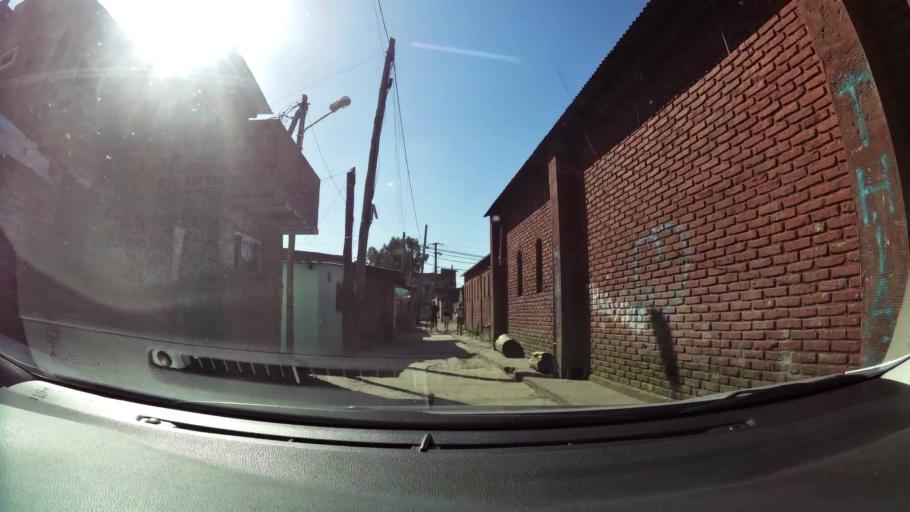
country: AR
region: Buenos Aires F.D.
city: Villa Lugano
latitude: -34.7073
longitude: -58.4879
